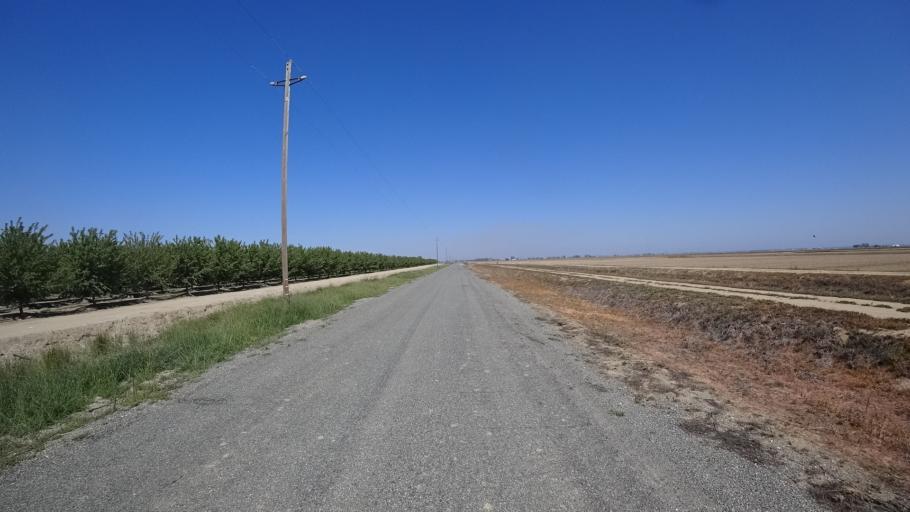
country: US
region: California
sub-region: Glenn County
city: Willows
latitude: 39.5111
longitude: -122.1026
